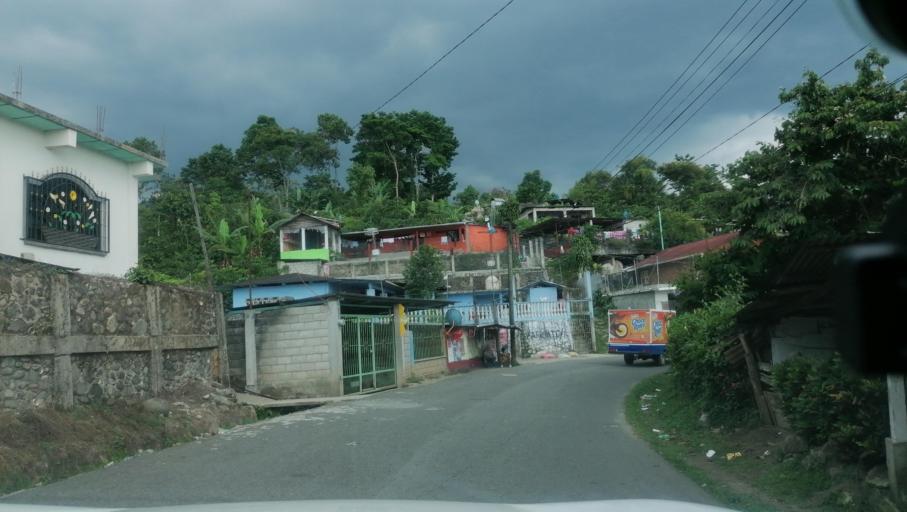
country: MX
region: Chiapas
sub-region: Cacahoatan
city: Benito Juarez
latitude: 15.0747
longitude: -92.1963
